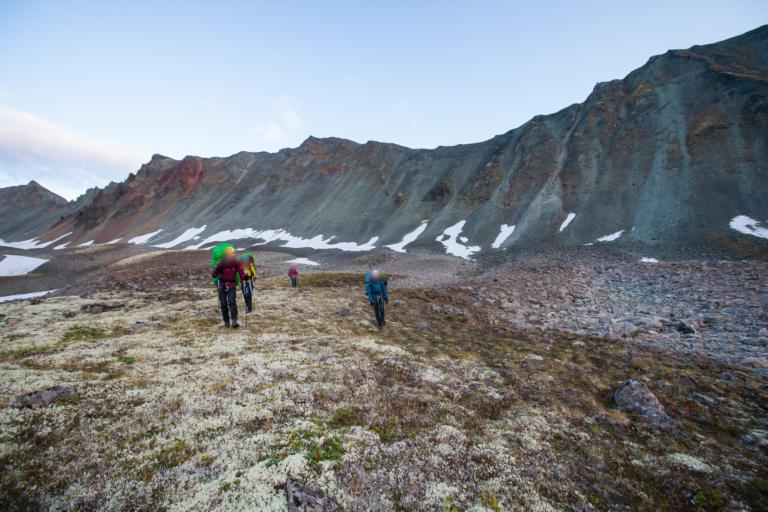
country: RU
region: Kamtsjatka
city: Yelizovo
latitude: 53.8641
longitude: 158.2040
